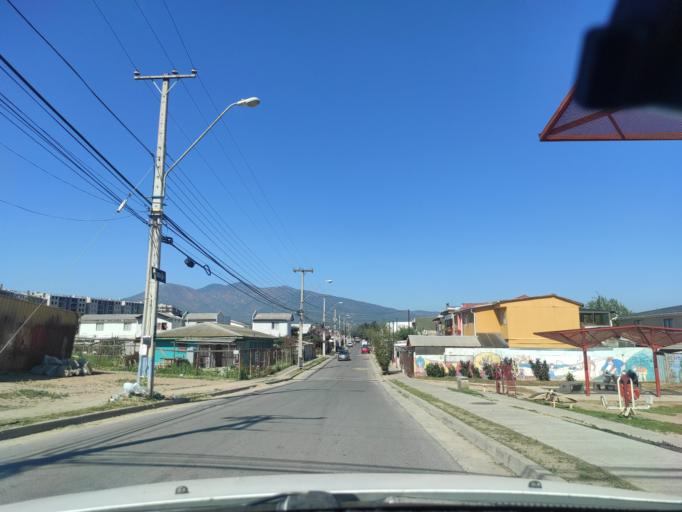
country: CL
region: Valparaiso
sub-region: Provincia de Marga Marga
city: Limache
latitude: -33.0157
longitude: -71.2627
